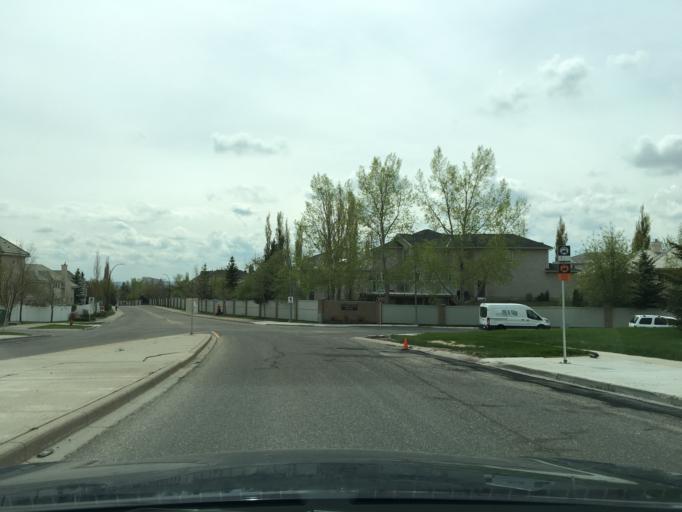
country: CA
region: Alberta
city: Calgary
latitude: 50.9390
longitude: -114.0854
